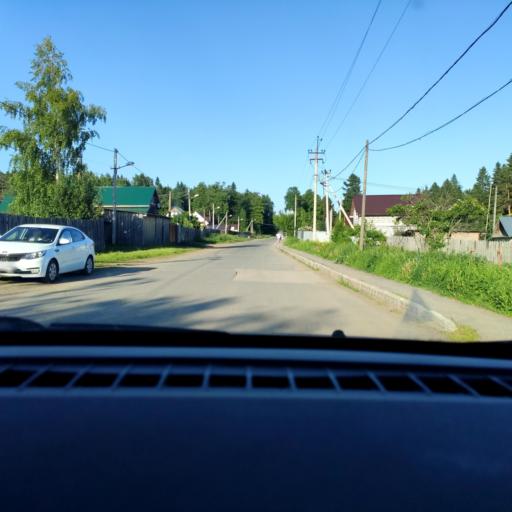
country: RU
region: Perm
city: Polazna
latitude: 58.1511
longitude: 56.4080
